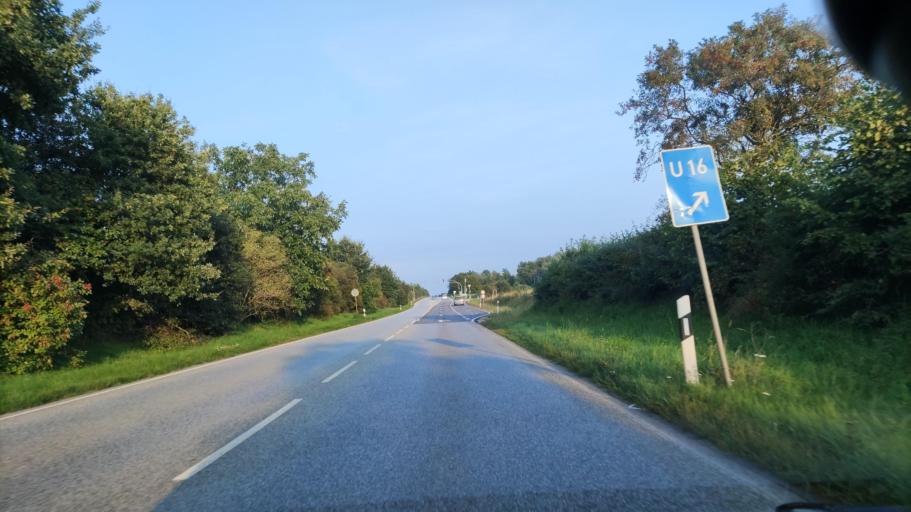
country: DE
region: Schleswig-Holstein
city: Grosshansdorf
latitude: 53.6426
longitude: 10.2687
